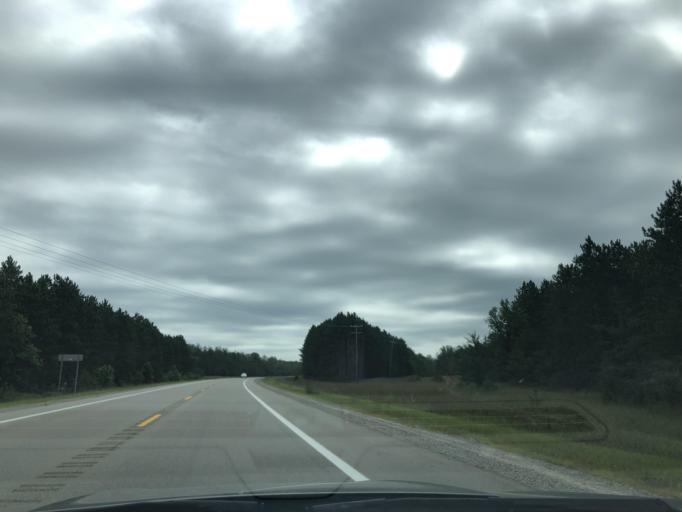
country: US
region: Michigan
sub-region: Clare County
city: Harrison
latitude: 44.0436
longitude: -85.0465
